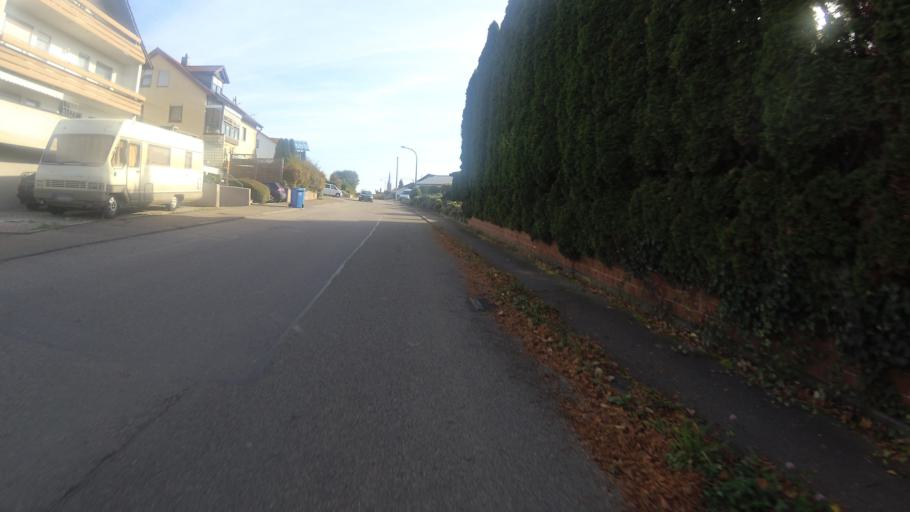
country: DE
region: Baden-Wuerttemberg
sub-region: Regierungsbezirk Stuttgart
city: Neudenau
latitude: 49.2634
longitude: 9.2934
